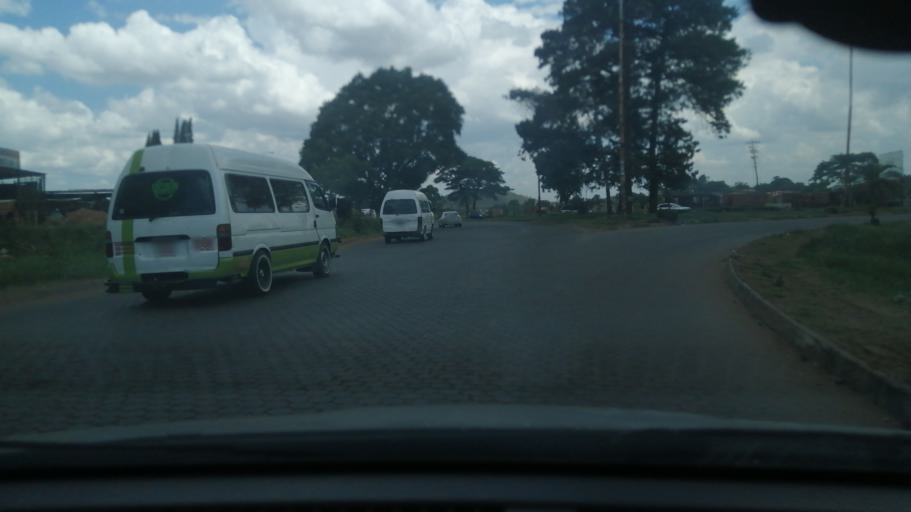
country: ZW
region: Harare
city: Harare
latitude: -17.8195
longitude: 30.9423
